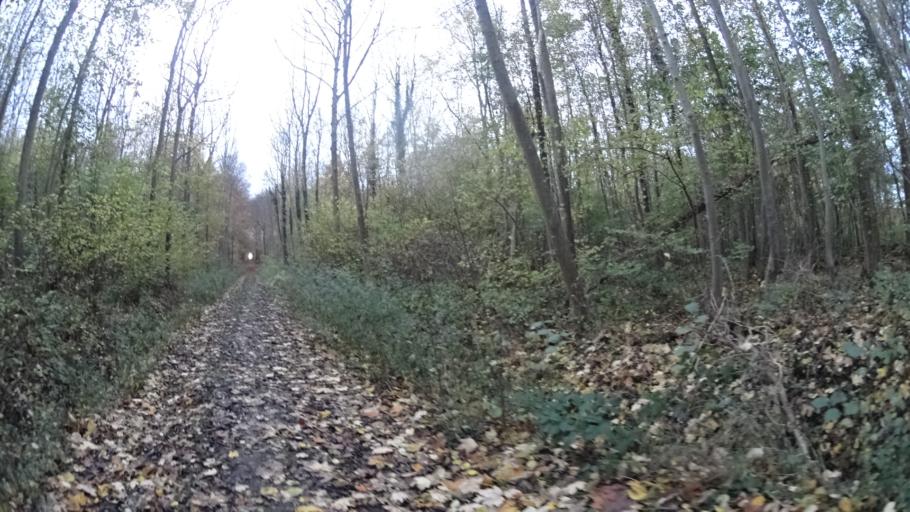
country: DK
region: Central Jutland
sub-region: Odder Kommune
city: Odder
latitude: 55.9036
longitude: 10.2286
